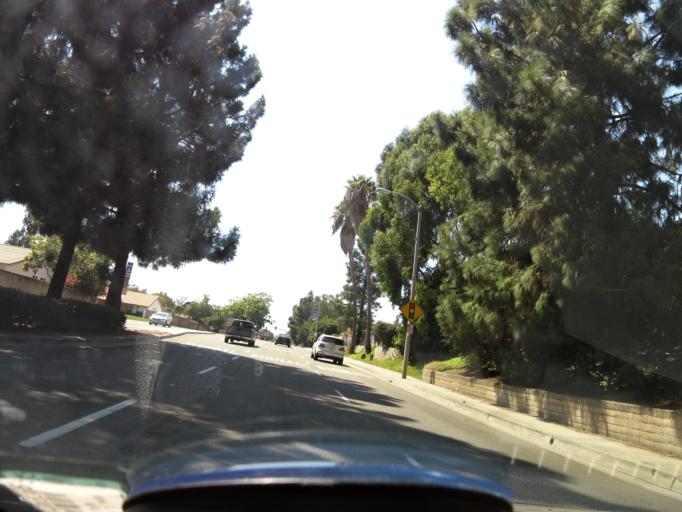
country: US
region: California
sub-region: Orange County
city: Yorba Linda
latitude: 33.8885
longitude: -117.8218
